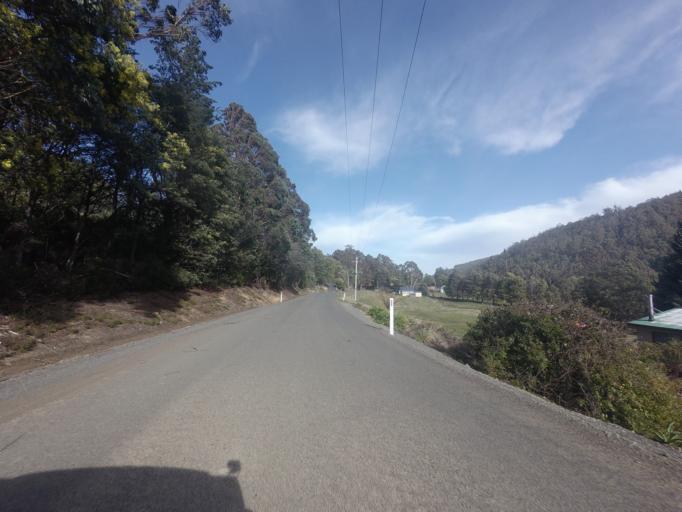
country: AU
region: Tasmania
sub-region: Huon Valley
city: Huonville
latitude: -43.0453
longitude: 147.1164
